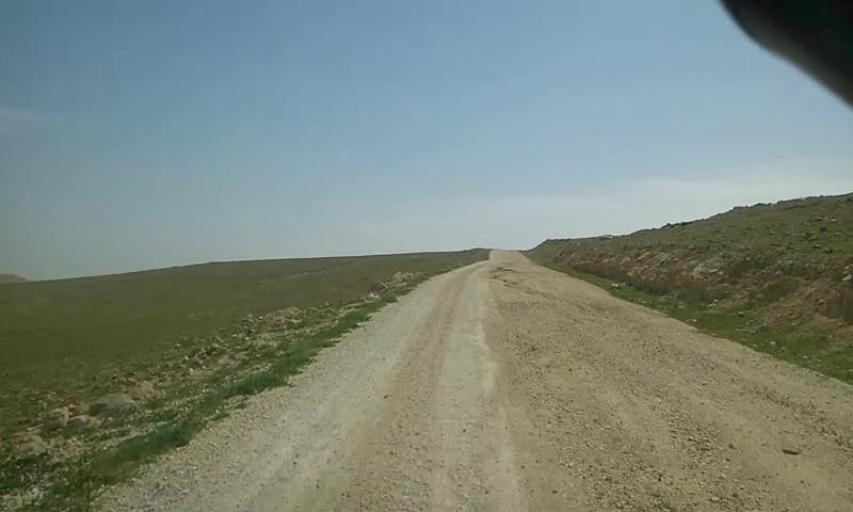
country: PS
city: `Arab ar Rashaydah
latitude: 31.5215
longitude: 35.2970
